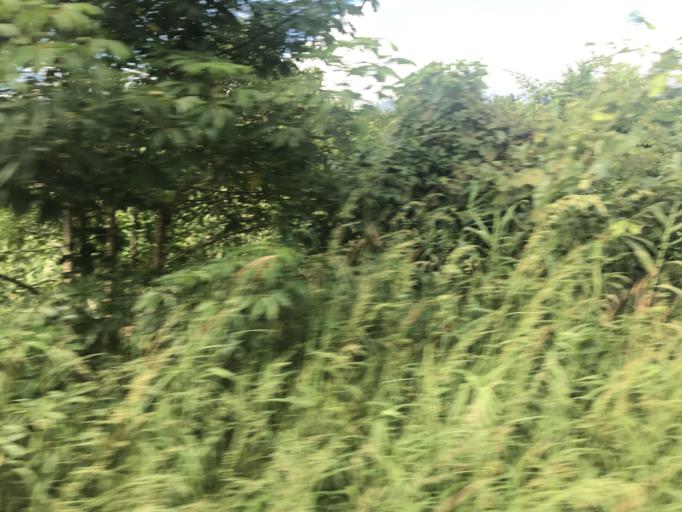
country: IN
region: Kerala
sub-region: Palakkad district
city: Palakkad
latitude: 10.8146
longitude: 76.6699
